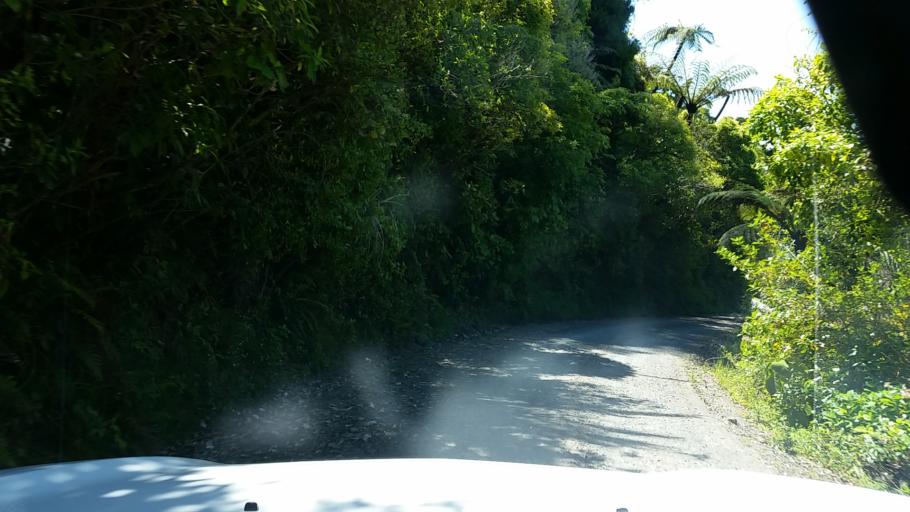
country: NZ
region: Auckland
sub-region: Auckland
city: Titirangi
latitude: -36.9288
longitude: 174.5815
